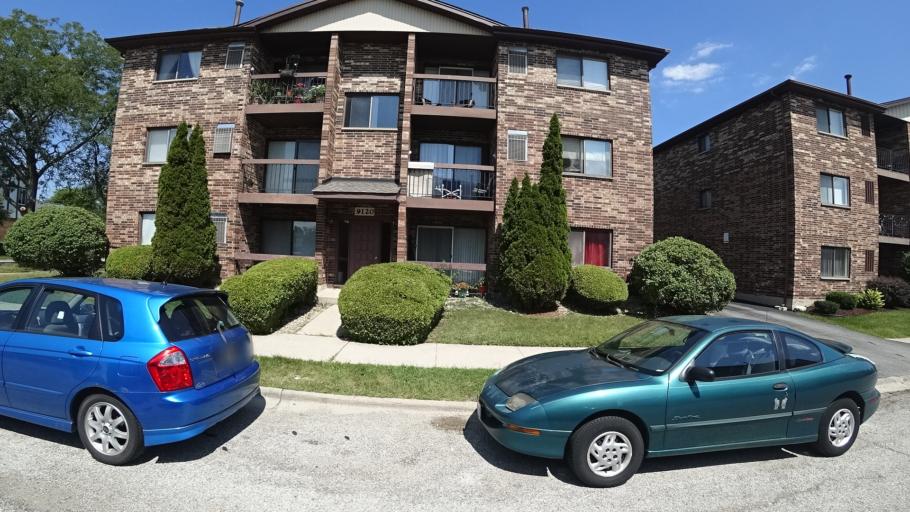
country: US
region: Illinois
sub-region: Cook County
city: Orland Park
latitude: 41.6193
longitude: -87.8401
